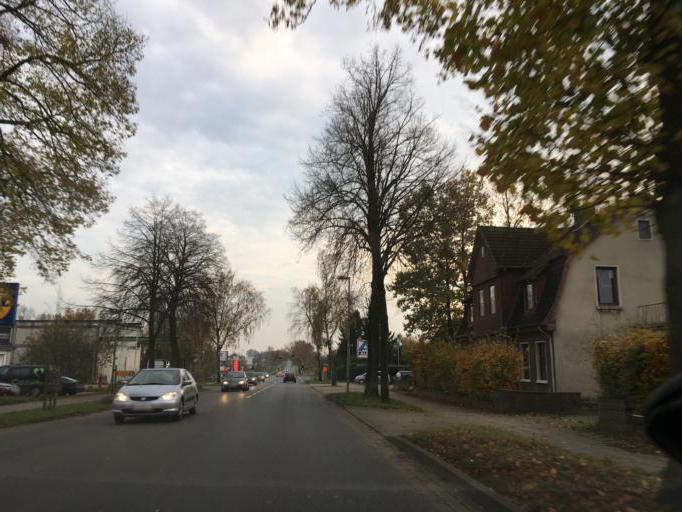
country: DE
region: Lower Saxony
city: Bergen
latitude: 52.8019
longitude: 9.9683
